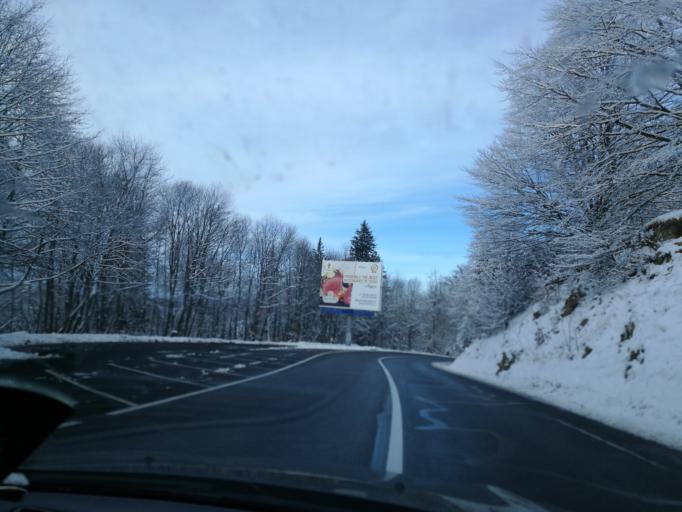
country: RO
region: Brasov
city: Brasov
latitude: 45.6004
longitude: 25.5529
